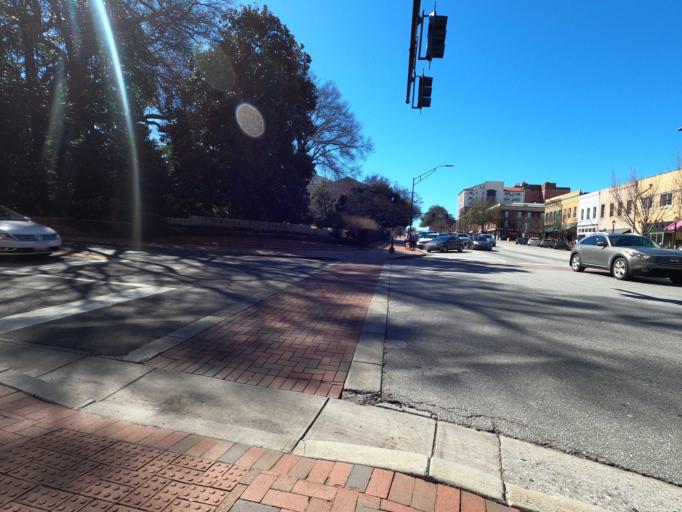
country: US
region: Georgia
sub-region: Clarke County
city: Athens
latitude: 33.9579
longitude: -83.3743
